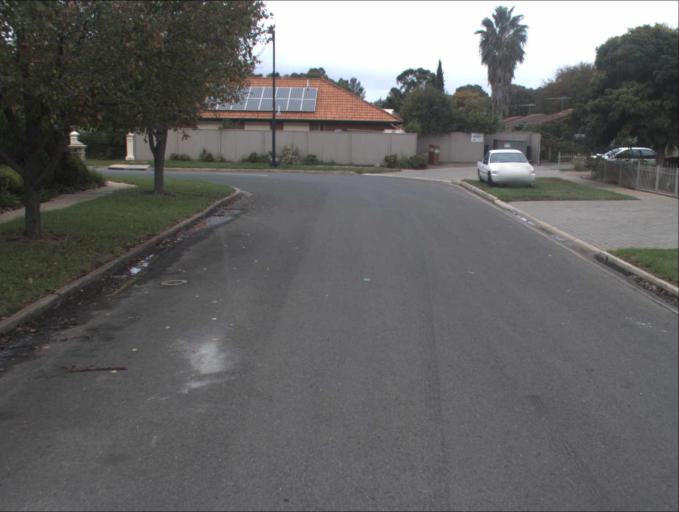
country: AU
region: South Australia
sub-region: Charles Sturt
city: Woodville
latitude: -34.8680
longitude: 138.5629
